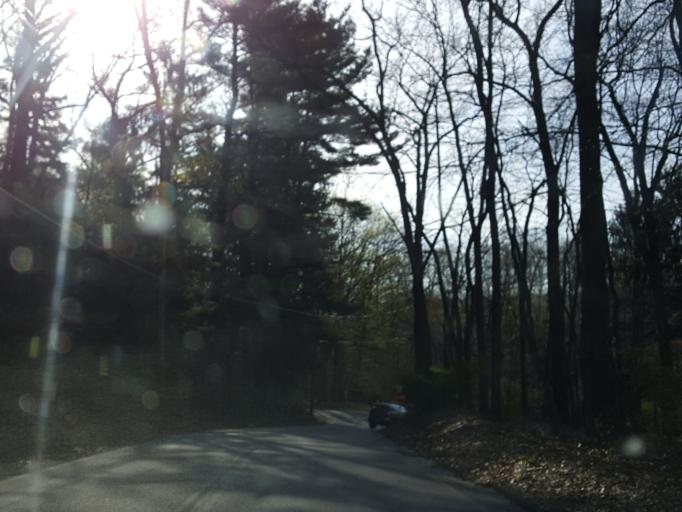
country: US
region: Pennsylvania
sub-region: Lebanon County
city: Cornwall
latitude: 40.2608
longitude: -76.4743
